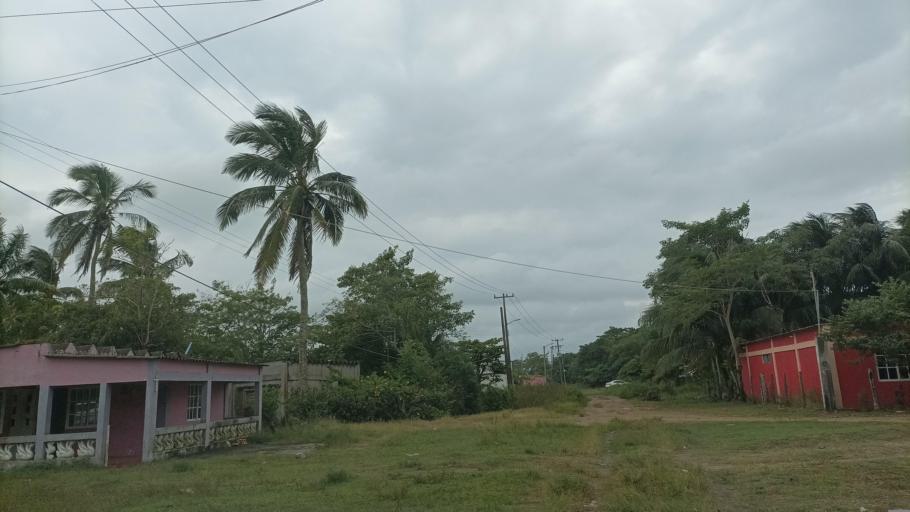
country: MX
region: Veracruz
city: Agua Dulce
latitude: 18.2069
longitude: -94.1399
